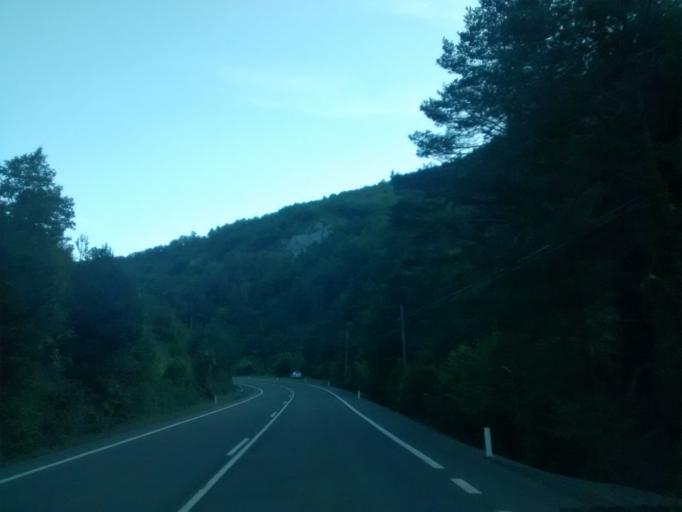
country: ES
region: Aragon
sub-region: Provincia de Huesca
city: Aragues del Puerto
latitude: 42.7004
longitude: -0.7469
